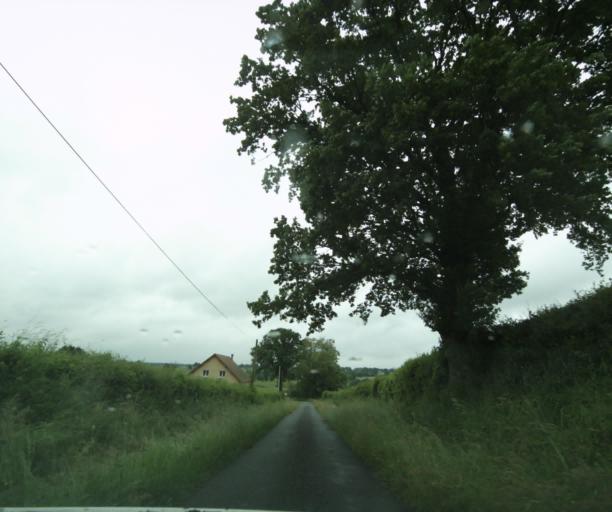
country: FR
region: Bourgogne
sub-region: Departement de Saone-et-Loire
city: Charolles
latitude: 46.4916
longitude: 4.2513
